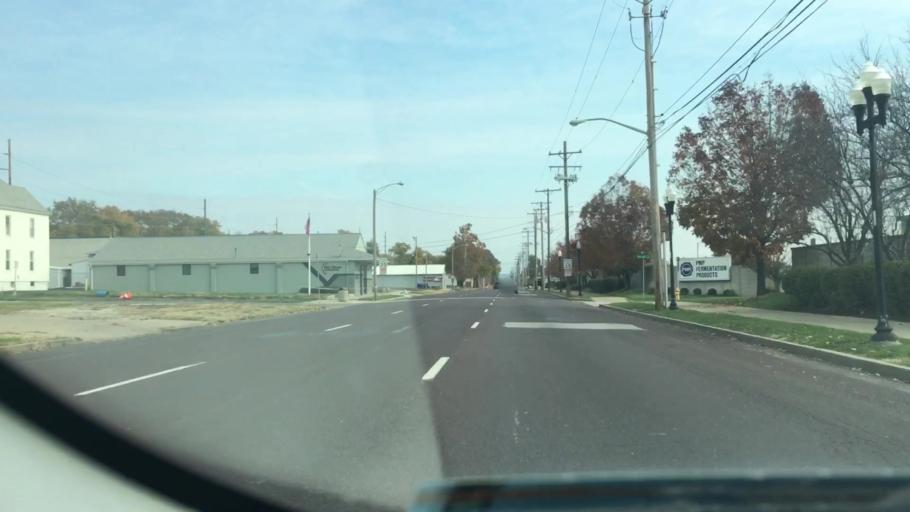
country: US
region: Illinois
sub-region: Peoria County
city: Peoria
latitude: 40.6977
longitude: -89.5805
